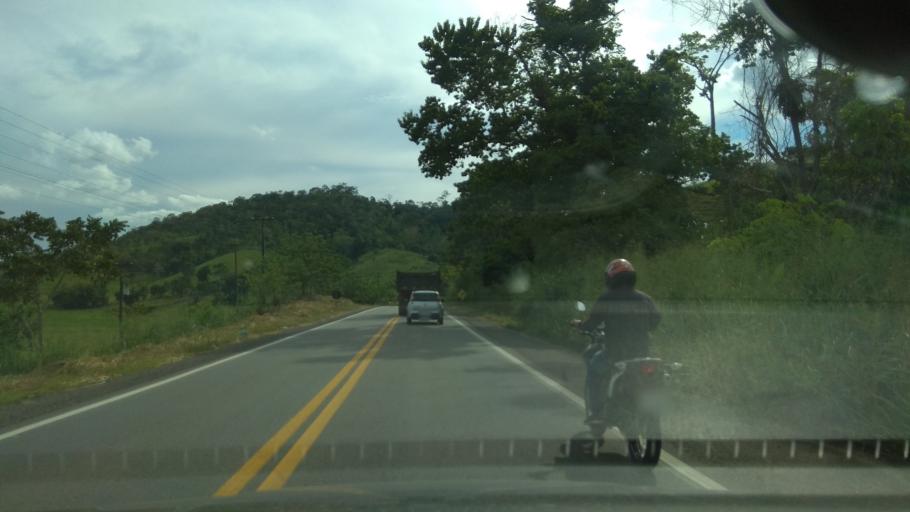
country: BR
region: Bahia
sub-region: Ipiau
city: Ipiau
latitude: -14.0967
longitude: -39.7791
